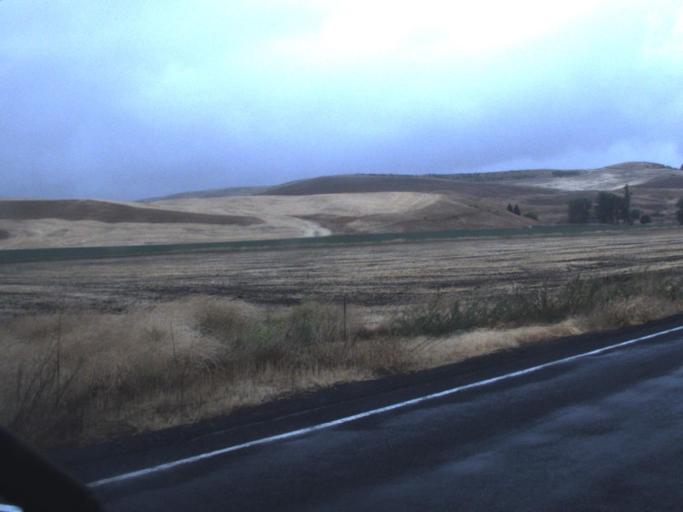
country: US
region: Washington
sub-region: Whitman County
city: Colfax
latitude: 47.0694
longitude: -117.5319
